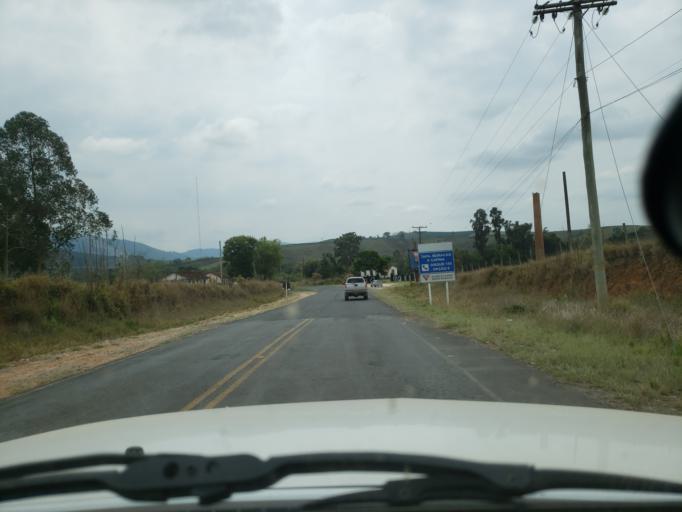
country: BR
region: Minas Gerais
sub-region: Jacutinga
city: Jacutinga
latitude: -22.2756
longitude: -46.6043
